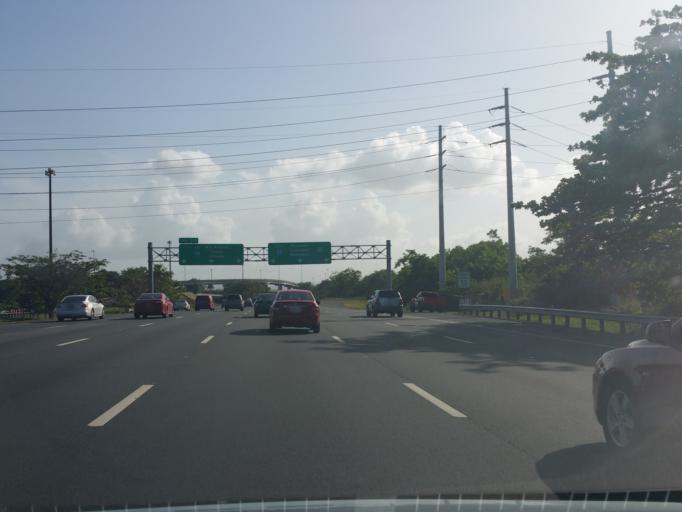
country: PR
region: Catano
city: Catano
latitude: 18.4334
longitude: -66.0740
